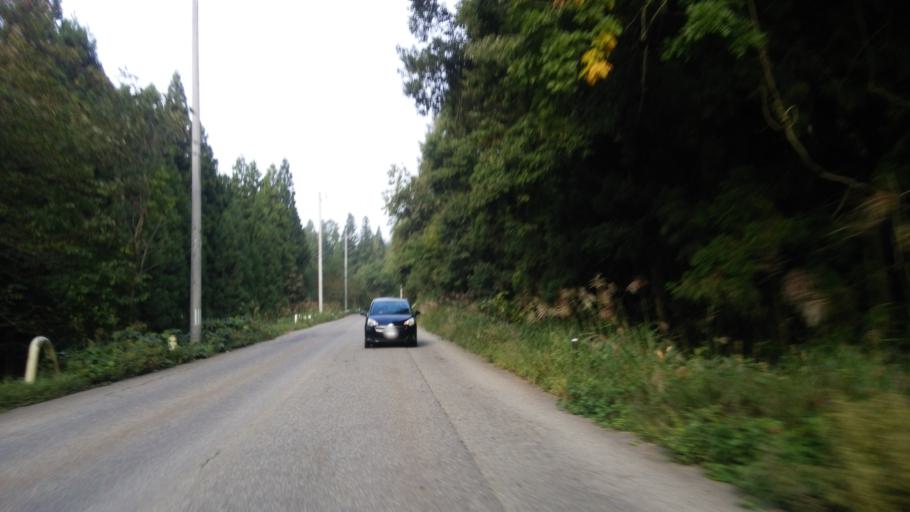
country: JP
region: Fukushima
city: Kitakata
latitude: 37.5733
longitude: 139.7827
